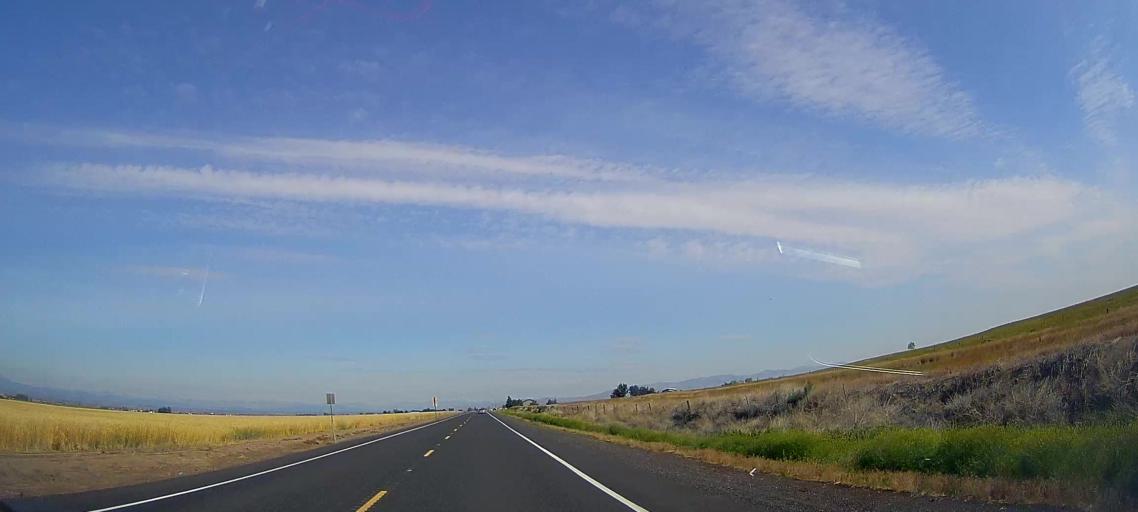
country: US
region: Oregon
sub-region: Jefferson County
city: Madras
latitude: 44.6705
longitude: -121.1401
